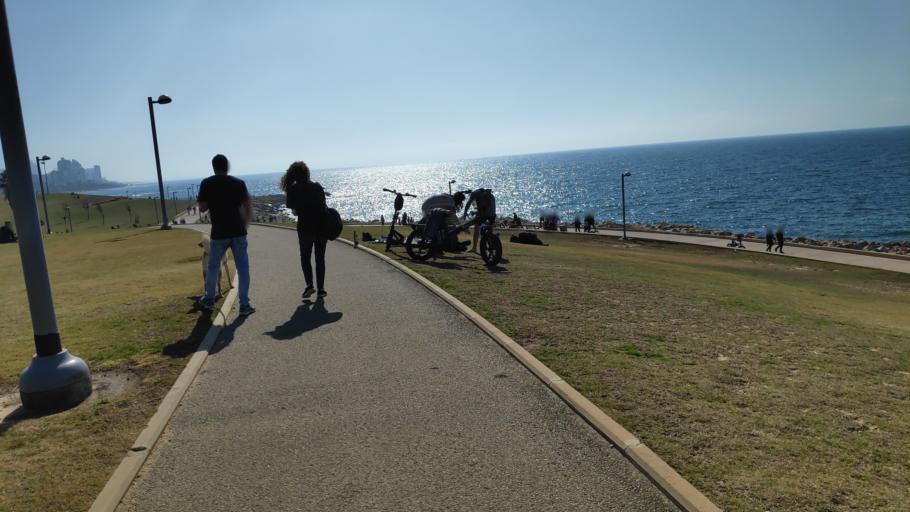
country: IL
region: Tel Aviv
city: Yafo
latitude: 32.0475
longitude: 34.7458
